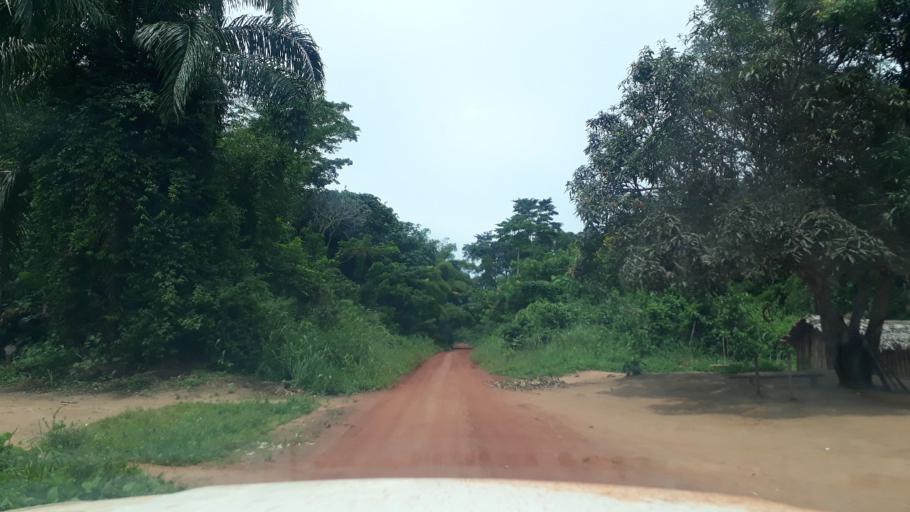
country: CD
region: Eastern Province
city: Aketi
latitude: 2.9334
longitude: 24.0937
